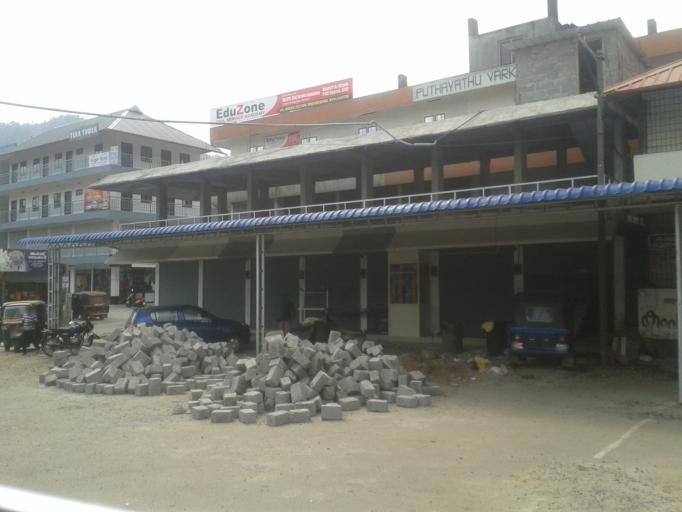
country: IN
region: Kerala
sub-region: Idukki
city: Munnar
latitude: 10.0150
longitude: 76.9531
